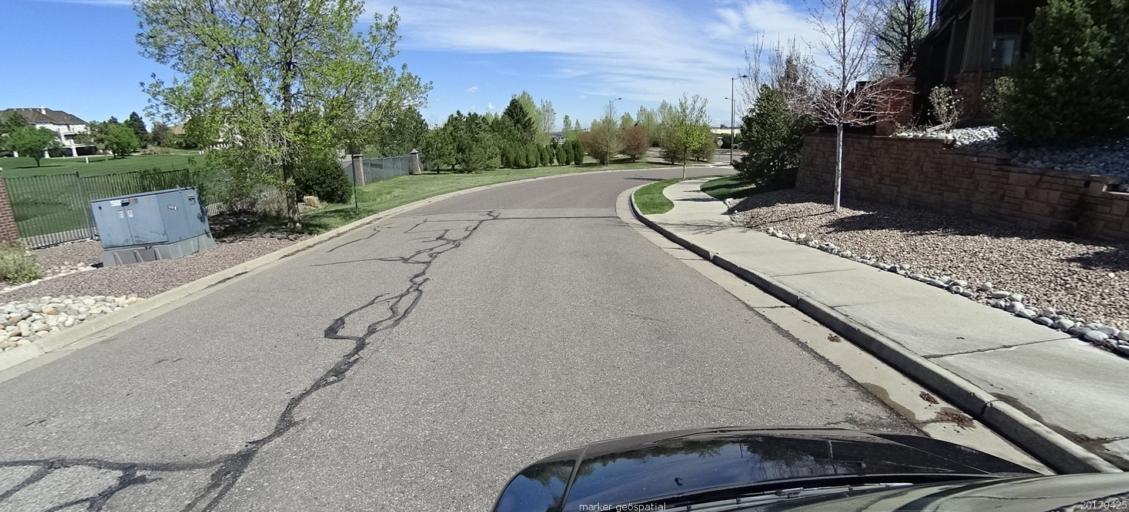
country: US
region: Colorado
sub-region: Douglas County
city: Carriage Club
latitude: 39.5331
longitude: -104.8857
